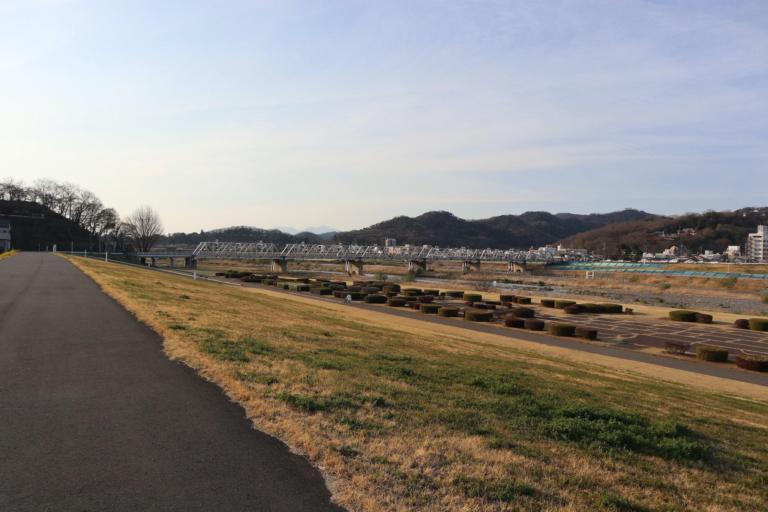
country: JP
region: Tochigi
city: Ashikaga
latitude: 36.3314
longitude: 139.4457
